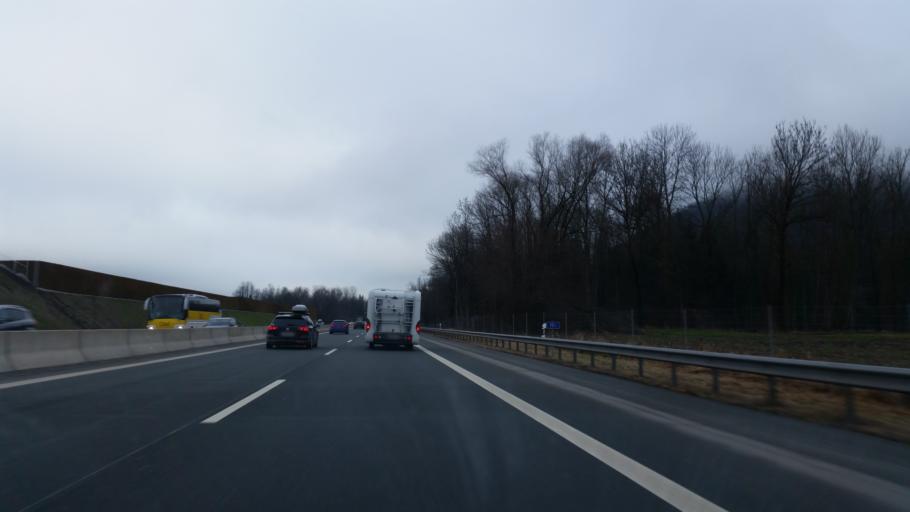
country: DE
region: Bavaria
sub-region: Upper Bavaria
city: Oberaudorf
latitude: 47.6523
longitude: 12.1867
